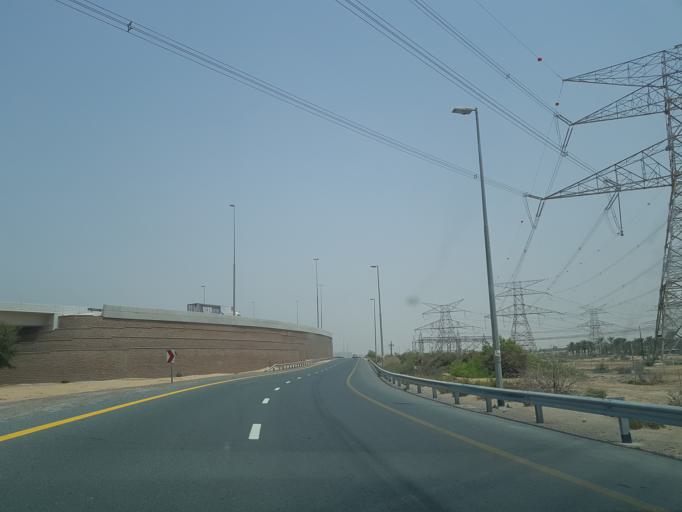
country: AE
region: Dubai
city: Dubai
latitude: 25.0849
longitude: 55.3948
